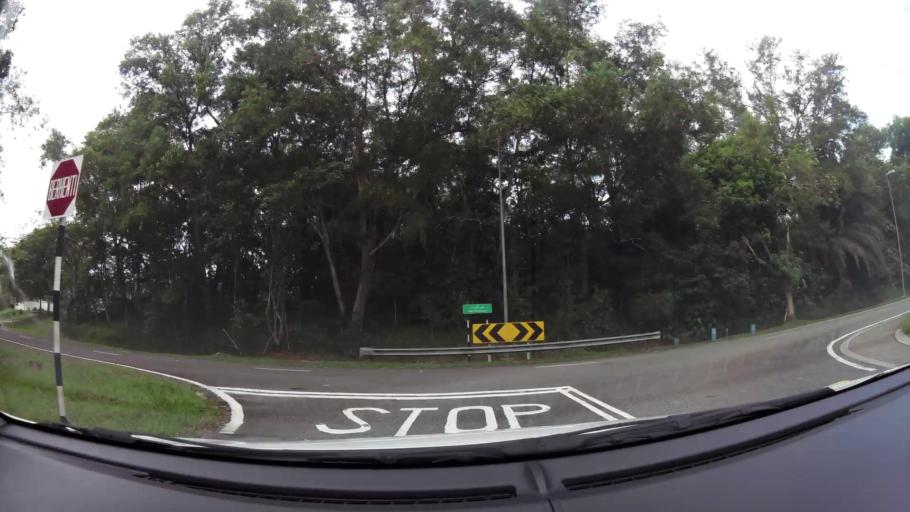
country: BN
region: Brunei and Muara
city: Bandar Seri Begawan
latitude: 4.8807
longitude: 114.9049
